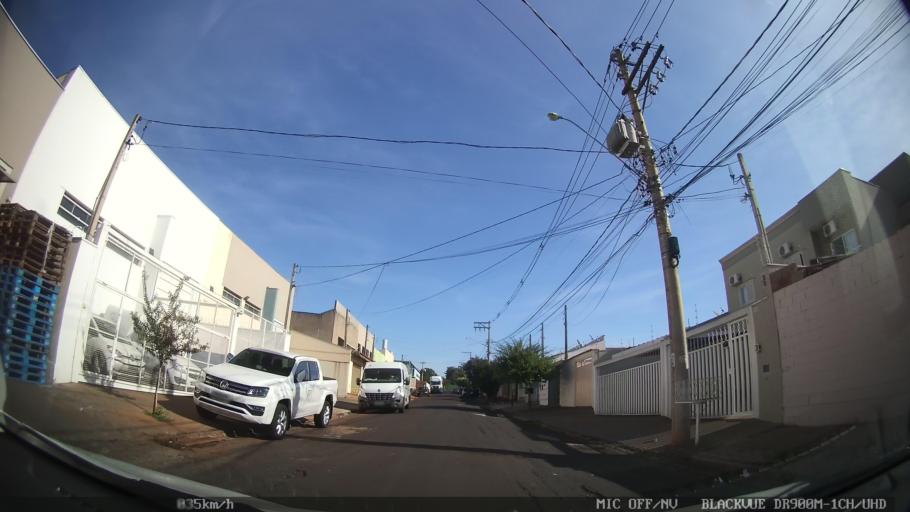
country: BR
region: Sao Paulo
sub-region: Ribeirao Preto
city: Ribeirao Preto
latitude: -21.1771
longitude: -47.7619
